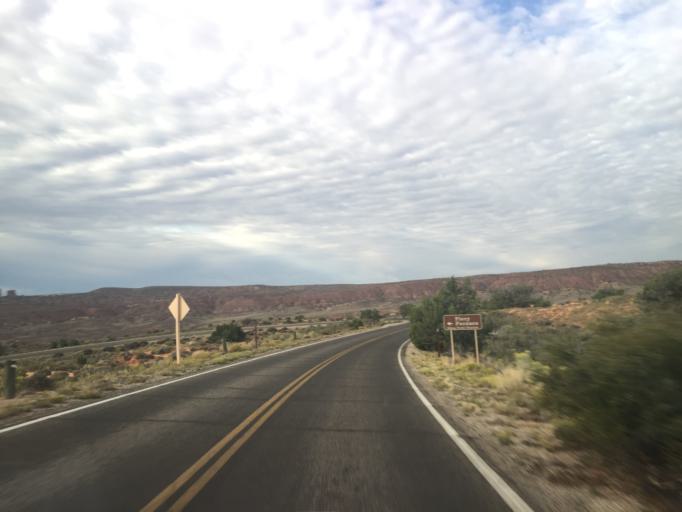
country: US
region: Utah
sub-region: Grand County
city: Moab
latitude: 38.7448
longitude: -109.5689
